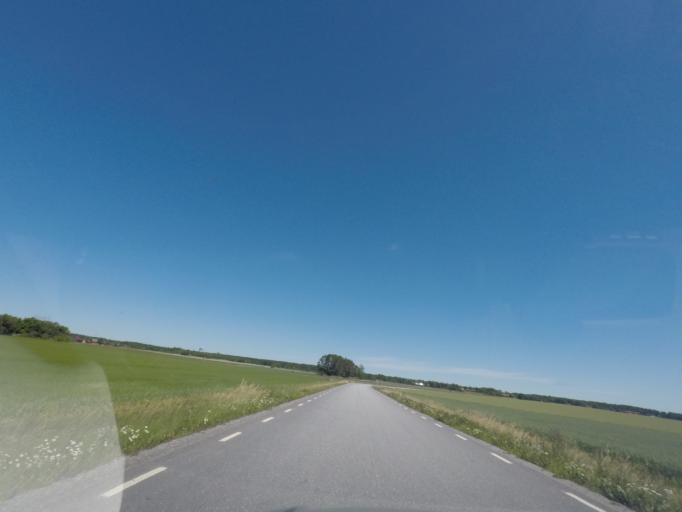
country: SE
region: Uppsala
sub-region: Enkopings Kommun
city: Enkoping
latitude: 59.7080
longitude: 17.0425
